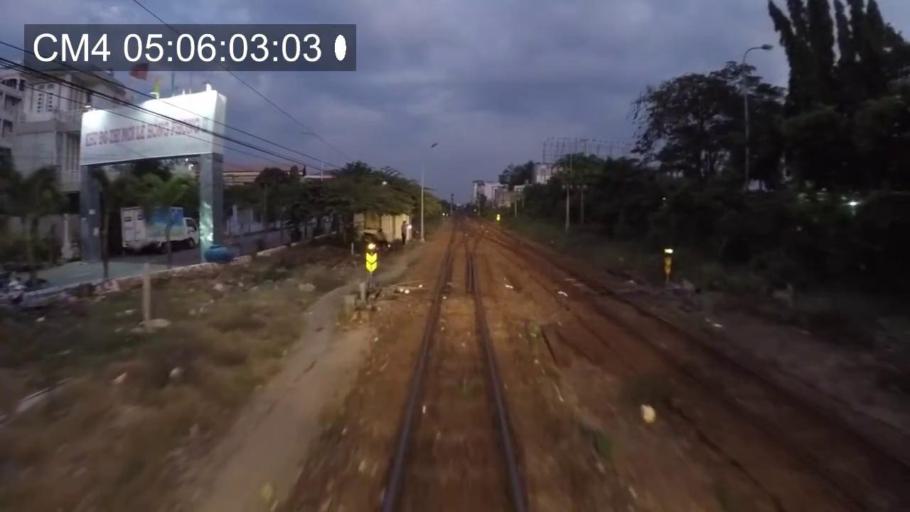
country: VN
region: Khanh Hoa
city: Nha Trang
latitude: 12.2748
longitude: 109.1780
